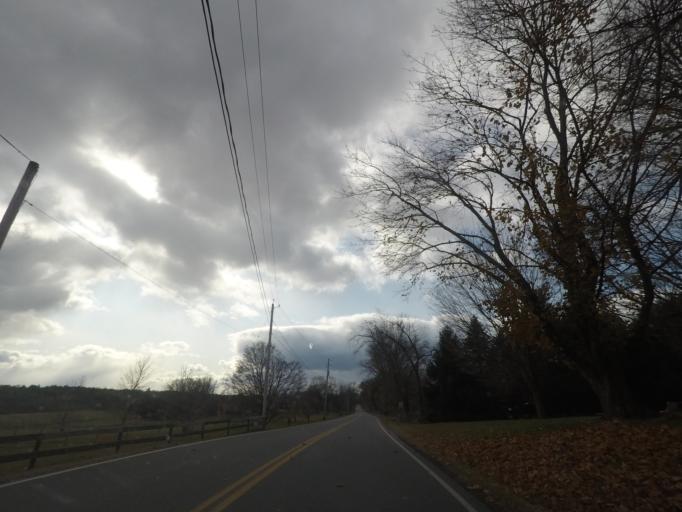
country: US
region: New York
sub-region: Saratoga County
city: Ballston Spa
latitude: 42.9860
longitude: -73.8200
